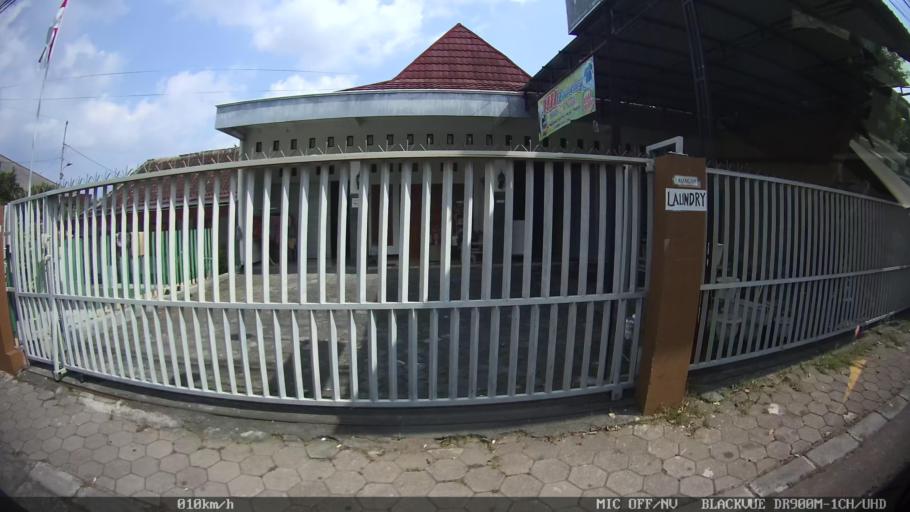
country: ID
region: Daerah Istimewa Yogyakarta
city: Yogyakarta
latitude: -7.8201
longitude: 110.3987
